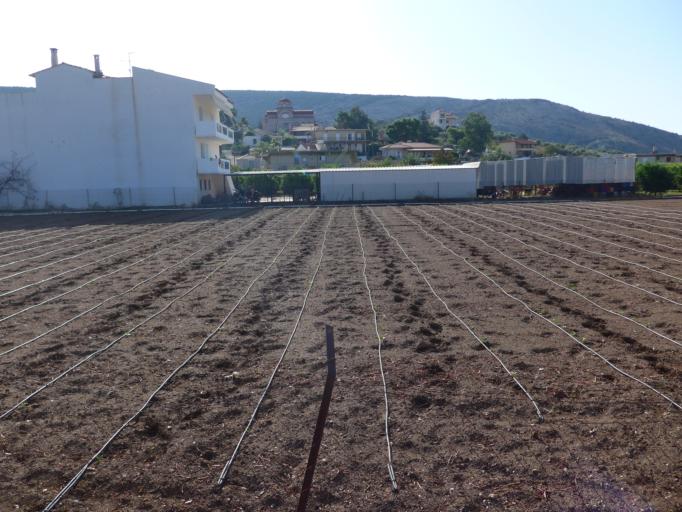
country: GR
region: Peloponnese
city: Asklipieio
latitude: 37.4880
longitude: 23.0098
